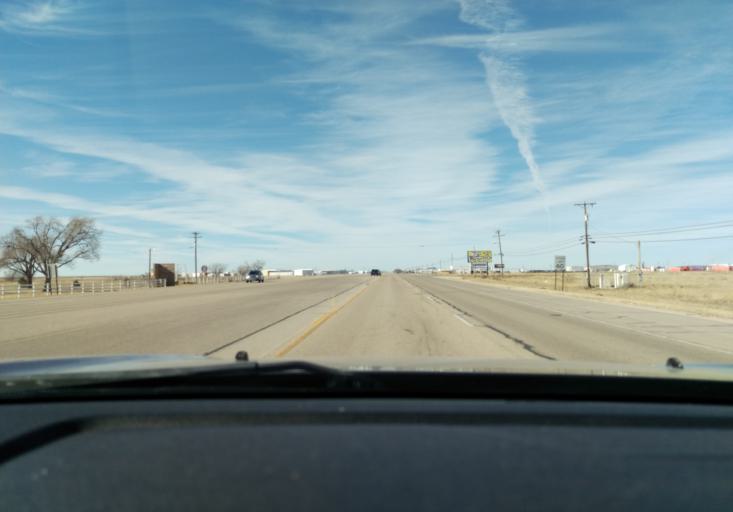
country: US
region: New Mexico
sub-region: Lea County
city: Hobbs
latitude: 32.6967
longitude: -103.2019
